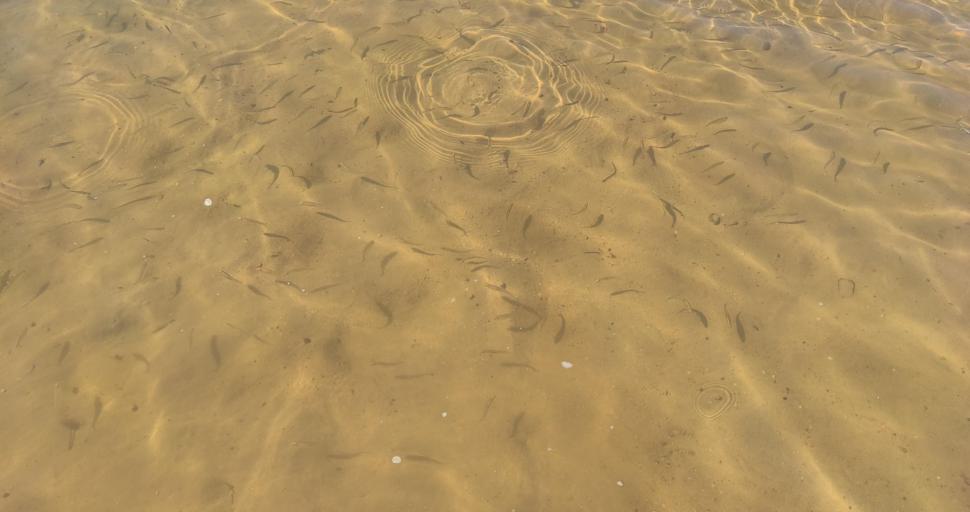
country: AR
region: Corrientes
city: Ituzaingo
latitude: -27.6025
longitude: -56.7630
